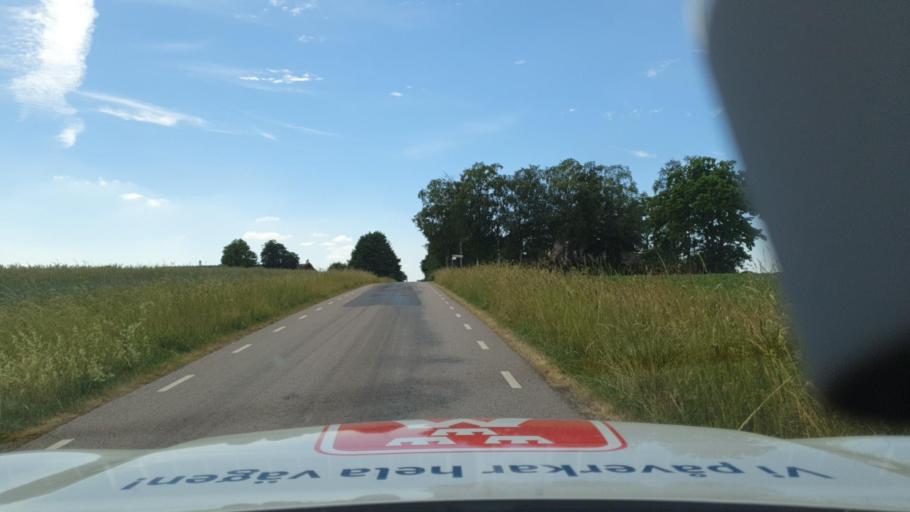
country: SE
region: Skane
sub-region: Sjobo Kommun
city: Sjoebo
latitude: 55.6320
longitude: 13.8302
